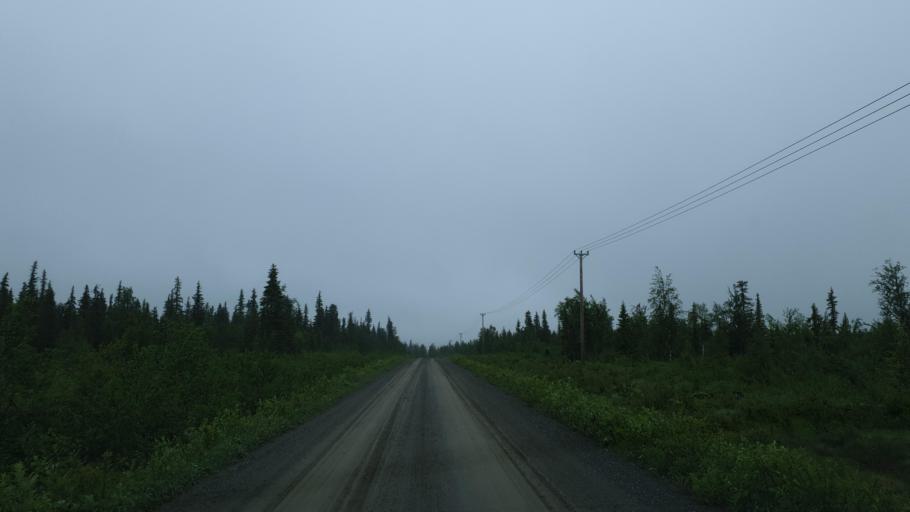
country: SE
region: Vaesterbotten
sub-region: Vilhelmina Kommun
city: Sjoberg
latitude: 65.3133
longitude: 15.9633
